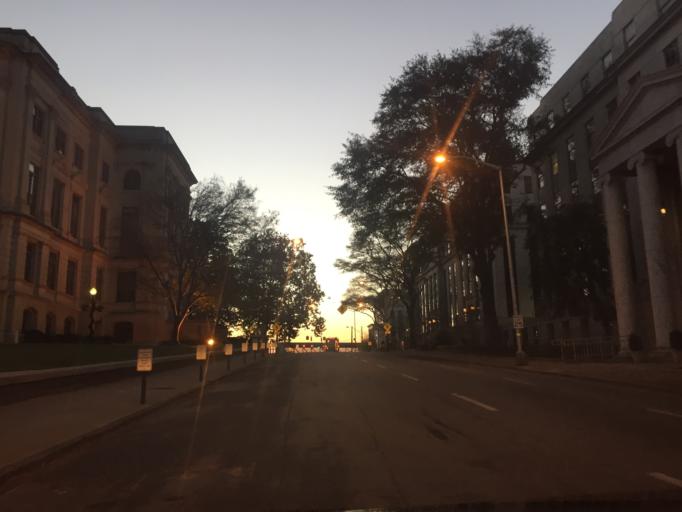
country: US
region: Georgia
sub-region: Fulton County
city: Atlanta
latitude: 33.7489
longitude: -84.3892
